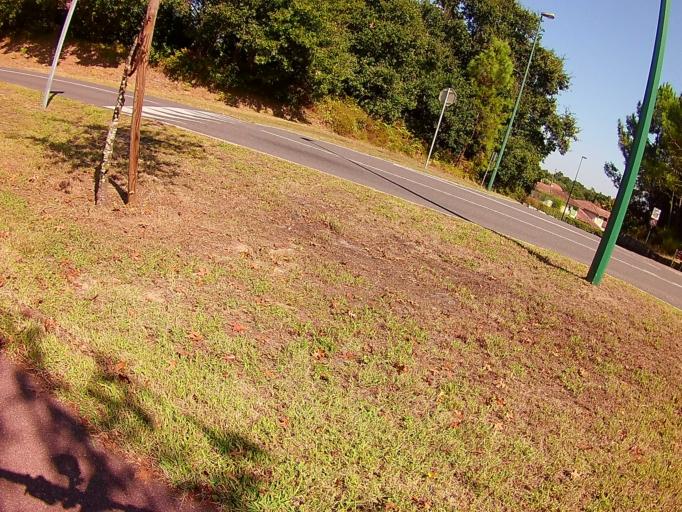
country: FR
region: Aquitaine
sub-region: Departement des Landes
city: Labenne
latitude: 43.5973
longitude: -1.4331
